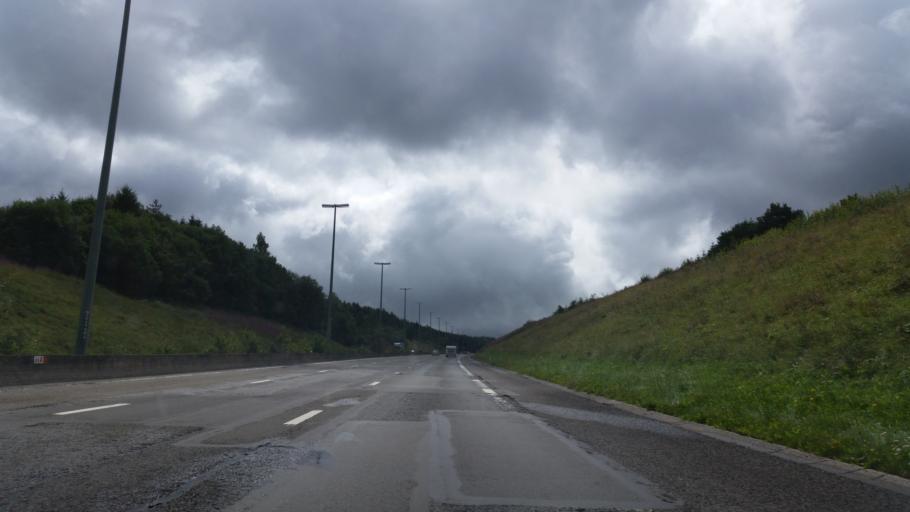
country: BE
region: Wallonia
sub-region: Province du Luxembourg
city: Manhay
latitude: 50.2838
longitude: 5.7278
